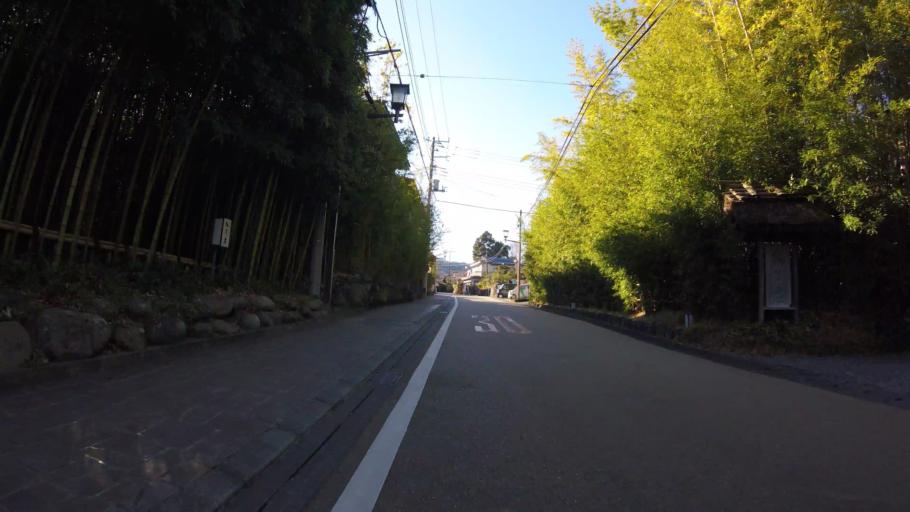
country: JP
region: Shizuoka
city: Heda
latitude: 34.9701
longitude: 138.9208
